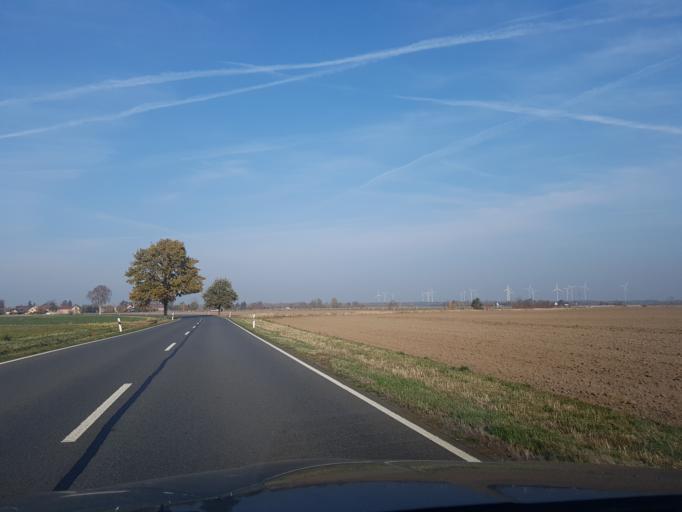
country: DE
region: Brandenburg
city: Falkenberg
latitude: 51.5353
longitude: 13.2888
